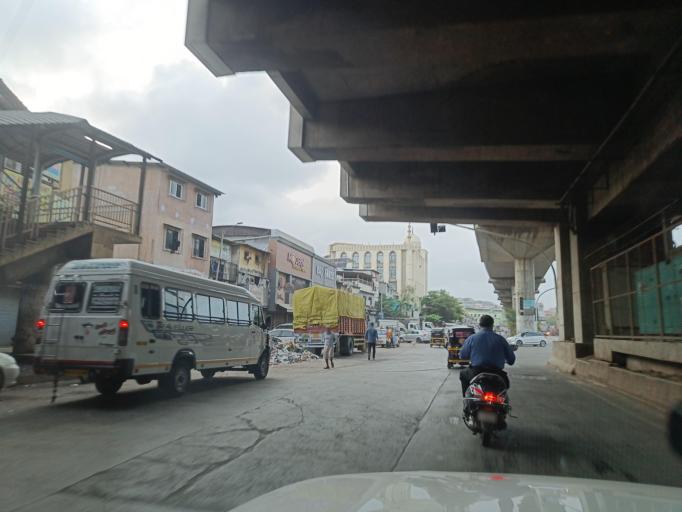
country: IN
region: Maharashtra
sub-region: Mumbai Suburban
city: Powai
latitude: 19.1034
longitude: 72.8883
